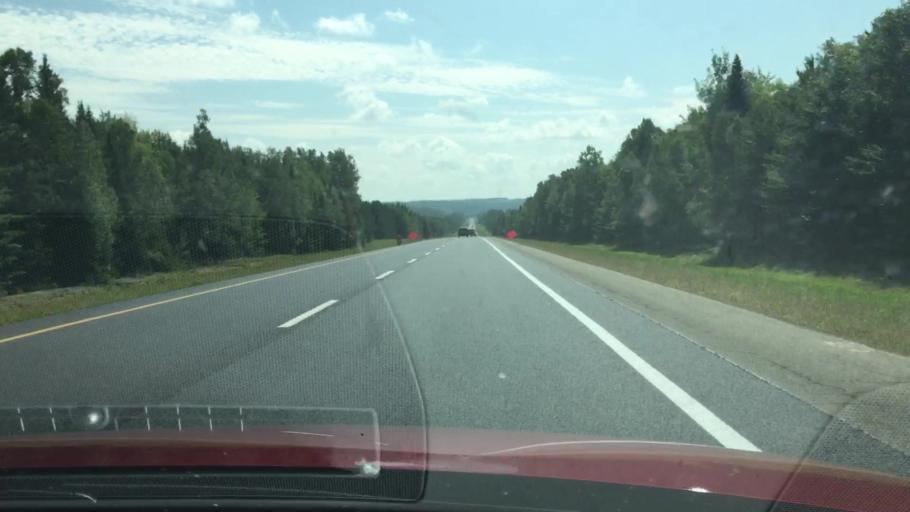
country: US
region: Maine
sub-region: Penobscot County
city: Patten
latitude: 45.8329
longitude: -68.4334
